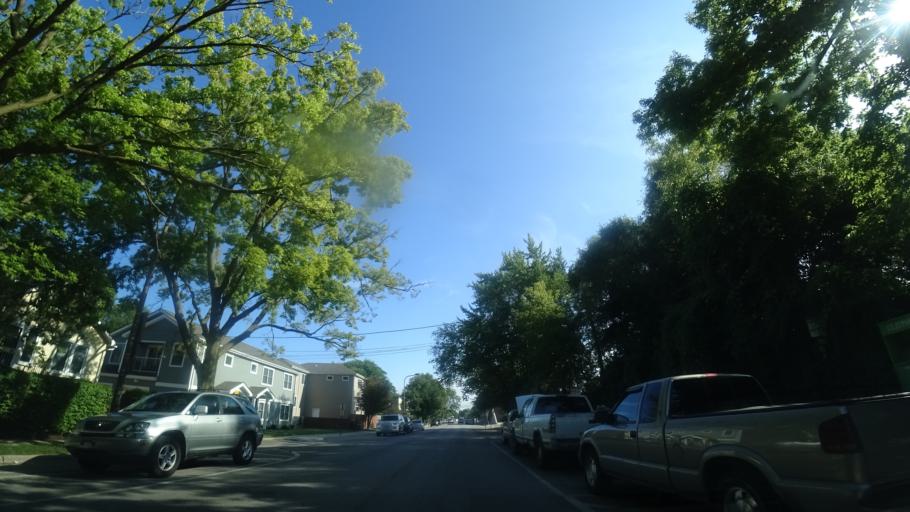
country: US
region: Illinois
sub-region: Cook County
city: Evanston
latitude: 42.0435
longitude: -87.6991
